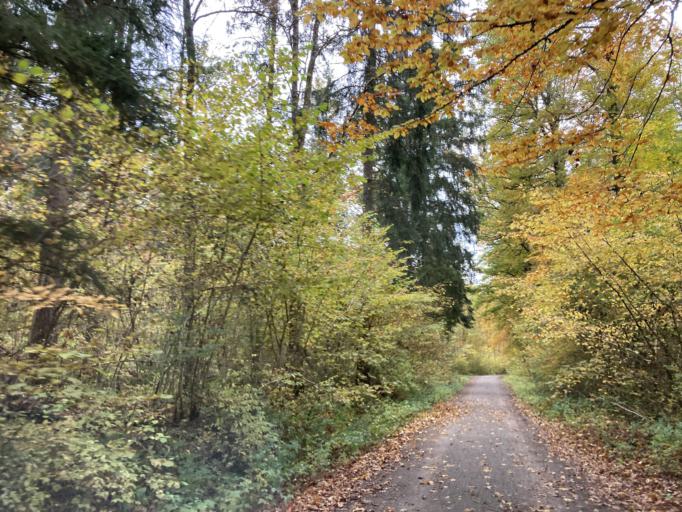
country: DE
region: Baden-Wuerttemberg
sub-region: Tuebingen Region
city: Dusslingen
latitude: 48.4641
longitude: 8.9971
